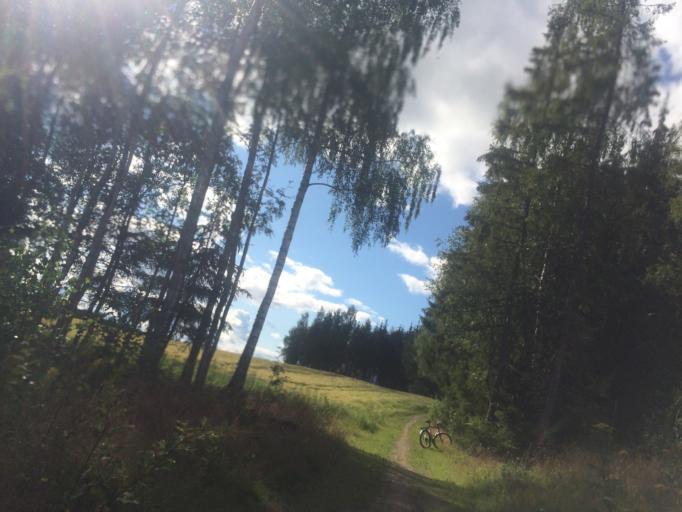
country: NO
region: Akershus
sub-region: As
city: As
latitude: 59.6729
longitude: 10.7911
